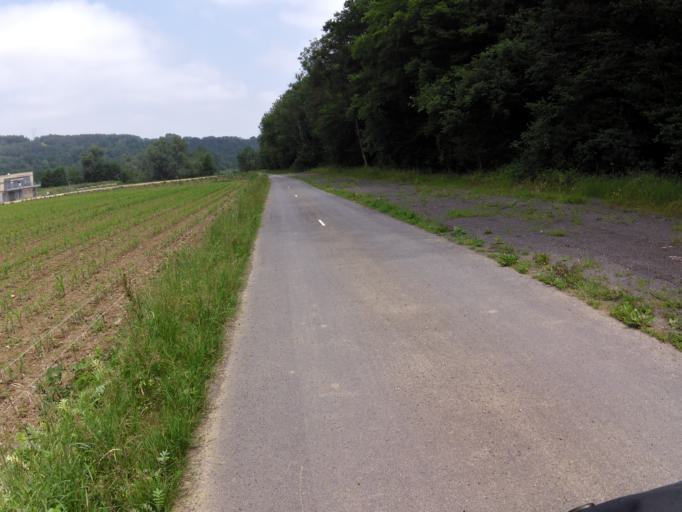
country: BE
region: Wallonia
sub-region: Province de Namur
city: Doische
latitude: 50.1096
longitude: 4.7720
